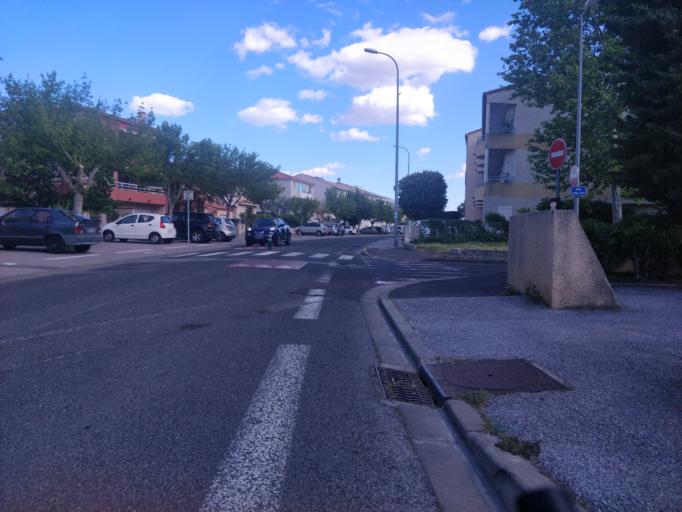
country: FR
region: Languedoc-Roussillon
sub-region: Departement des Pyrenees-Orientales
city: Perpignan
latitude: 42.6876
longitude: 2.9101
